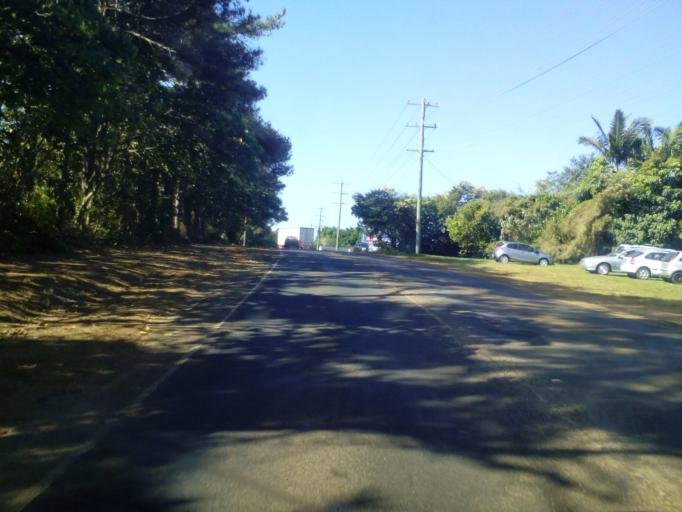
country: AU
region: New South Wales
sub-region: Tweed
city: Kingscliff
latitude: -28.2665
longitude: 153.5656
